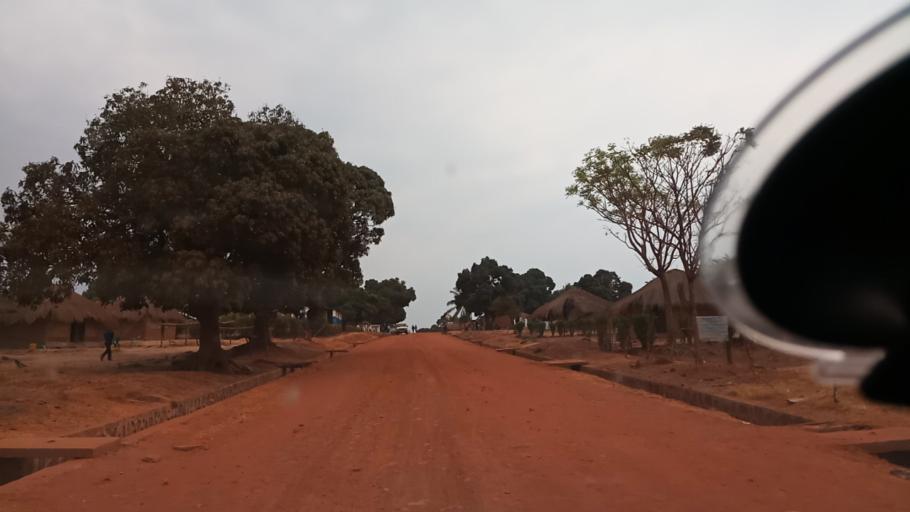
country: ZM
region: Luapula
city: Nchelenge
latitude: -9.1014
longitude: 28.3007
